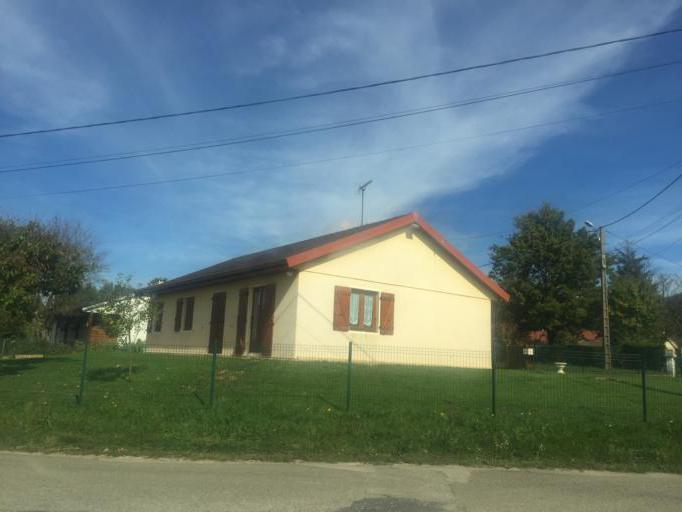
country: FR
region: Rhone-Alpes
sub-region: Departement de l'Ain
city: Marboz
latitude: 46.4128
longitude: 5.2658
